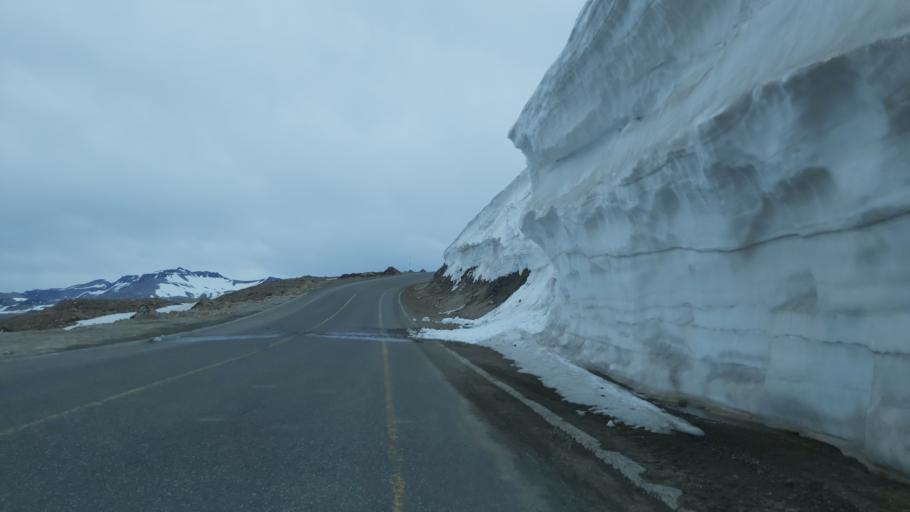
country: CL
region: Maule
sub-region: Provincia de Linares
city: Colbun
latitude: -36.0216
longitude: -70.5278
